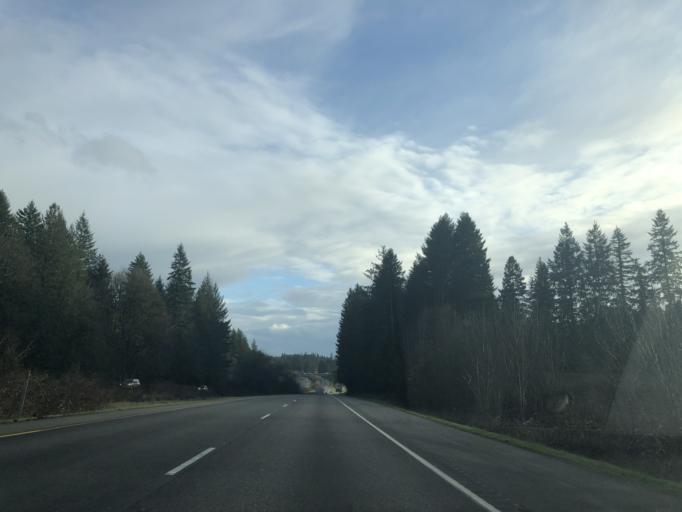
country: US
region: Washington
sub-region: Kitsap County
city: Bethel
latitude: 47.5092
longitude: -122.6509
